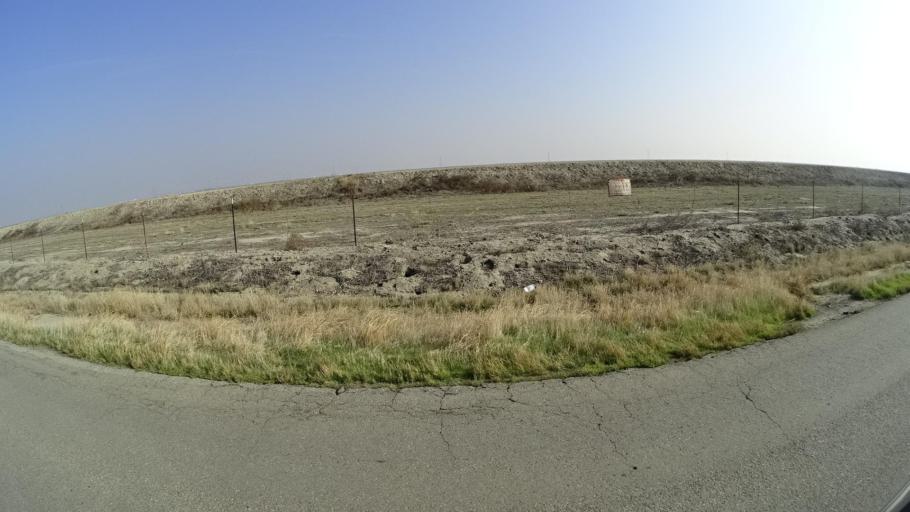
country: US
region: California
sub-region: Kern County
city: Buttonwillow
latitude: 35.3365
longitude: -119.3590
